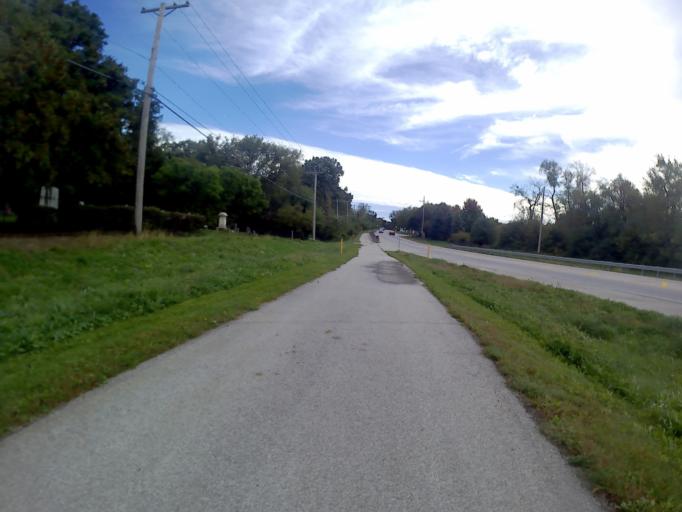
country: US
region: Illinois
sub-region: Kane County
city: South Elgin
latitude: 41.9742
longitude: -88.2663
